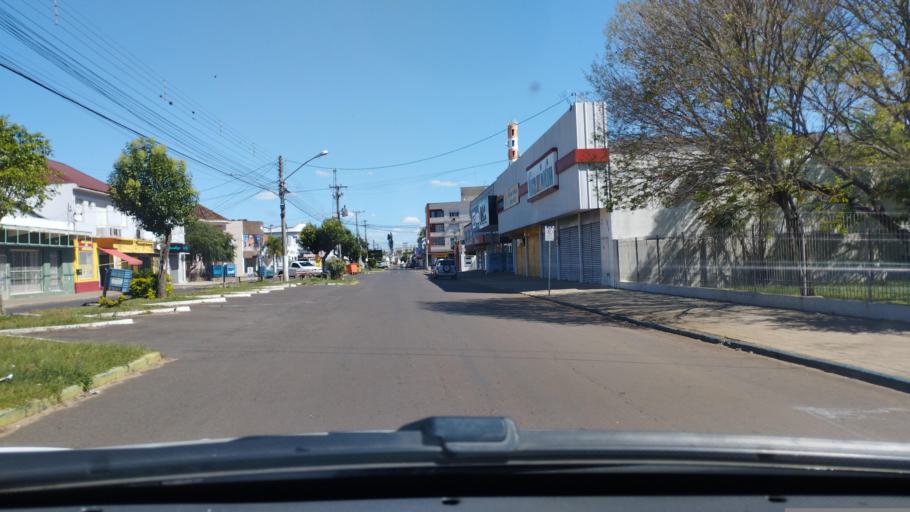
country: BR
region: Rio Grande do Sul
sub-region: Tupancireta
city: Tupancireta
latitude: -29.0788
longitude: -53.8379
